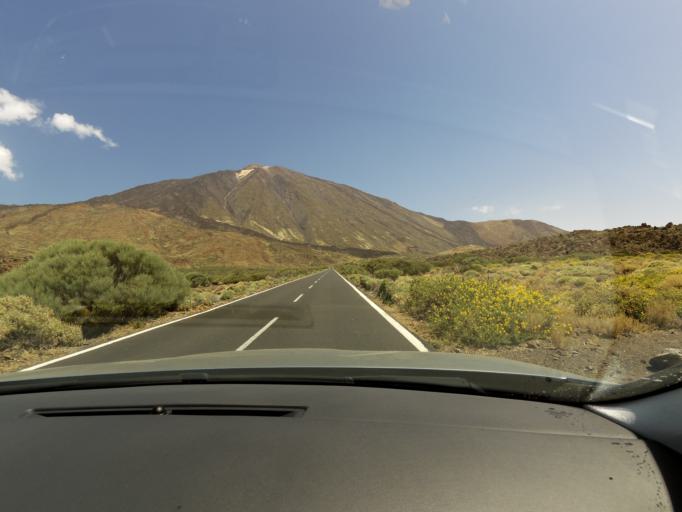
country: ES
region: Canary Islands
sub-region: Provincia de Santa Cruz de Tenerife
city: Vilaflor
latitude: 28.2339
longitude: -16.6294
